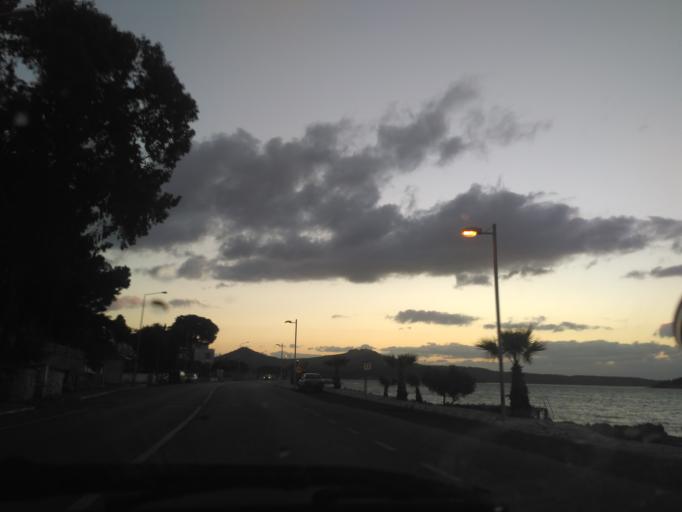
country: TR
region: Balikesir
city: Ayvalik
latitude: 39.3058
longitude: 26.6656
